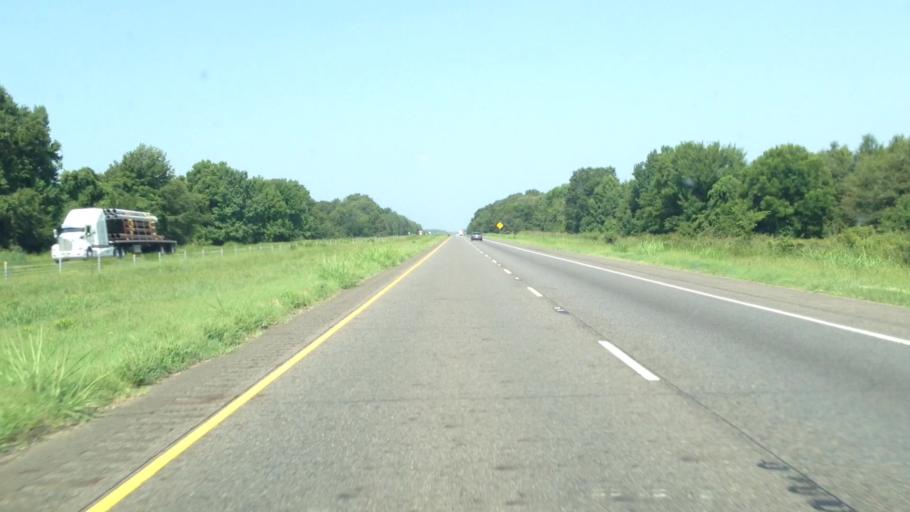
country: US
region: Louisiana
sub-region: Richland Parish
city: Delhi
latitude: 32.4343
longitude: -91.4375
